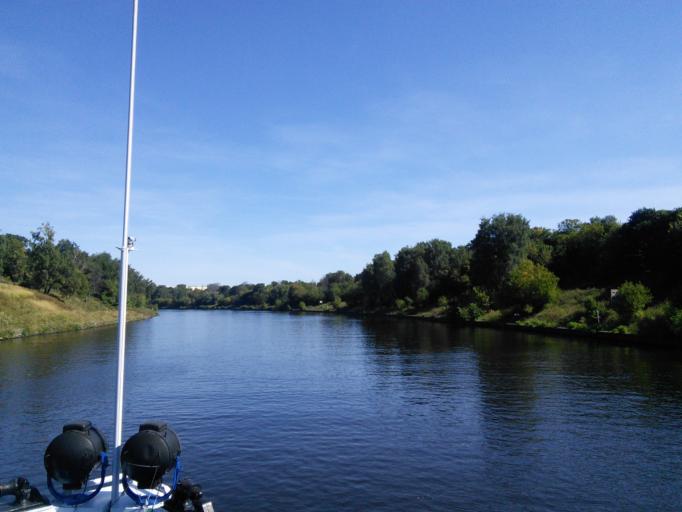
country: RU
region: Moskovskaya
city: Levoberezhnaya
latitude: 55.9136
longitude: 37.4832
